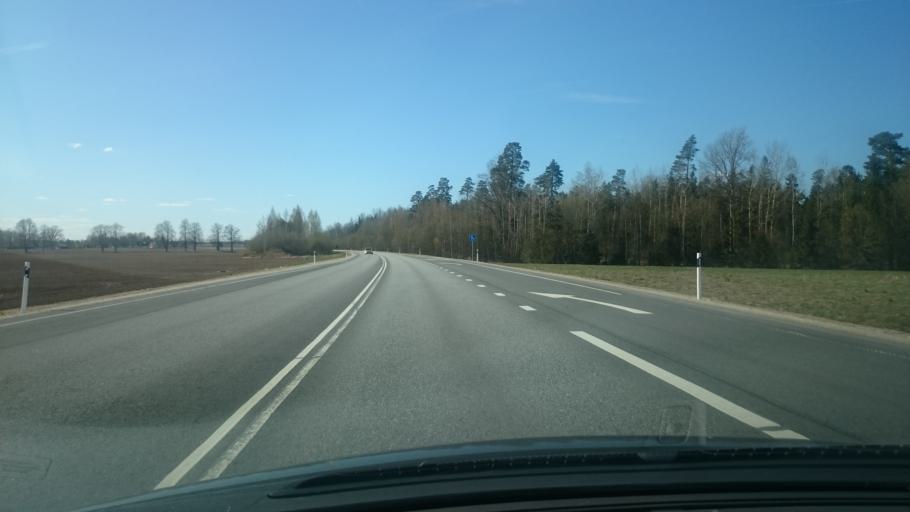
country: EE
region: Tartu
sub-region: Tartu linn
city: Tartu
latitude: 58.3682
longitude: 26.8828
